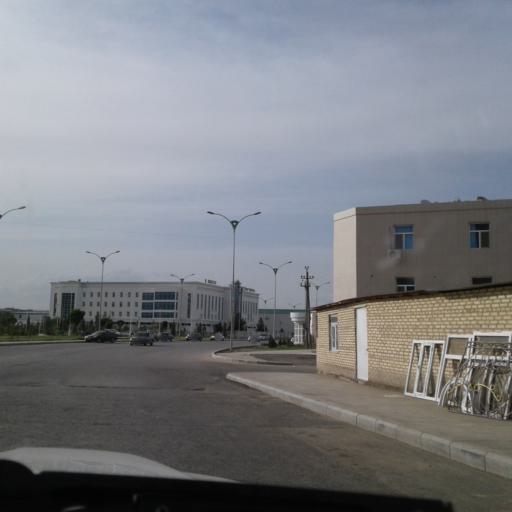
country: TM
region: Mary
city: Mary
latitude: 37.5808
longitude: 61.8715
